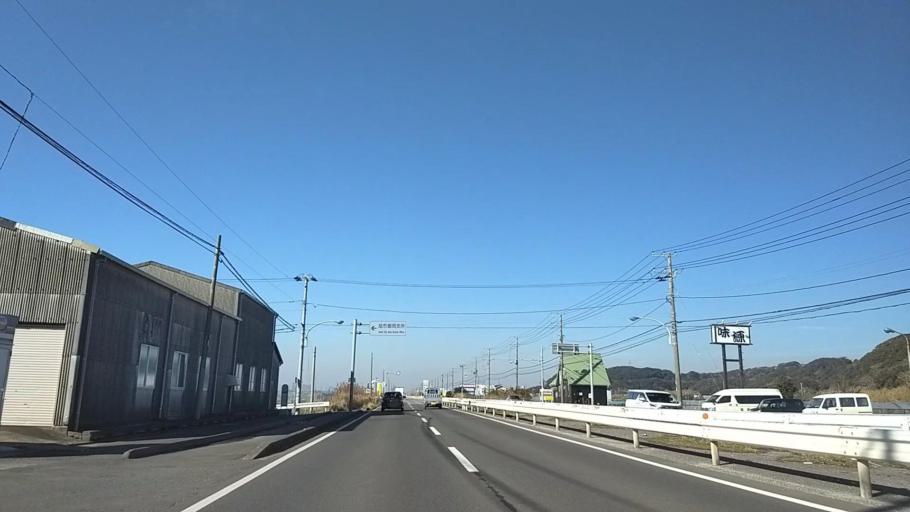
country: JP
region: Chiba
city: Asahi
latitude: 35.7107
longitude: 140.7168
